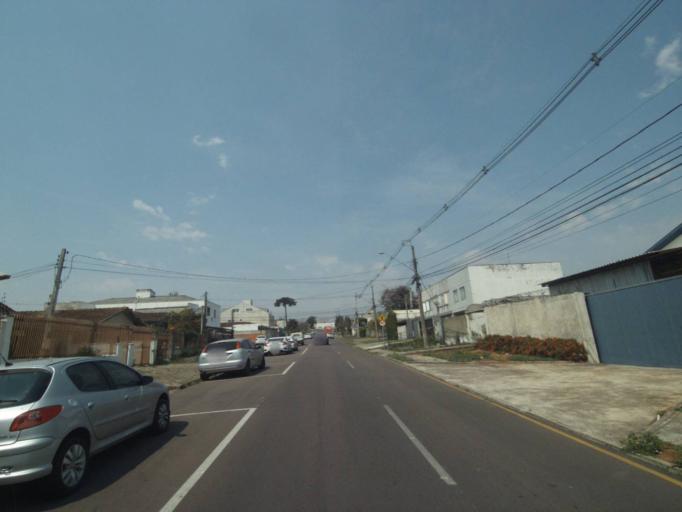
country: BR
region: Parana
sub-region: Curitiba
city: Curitiba
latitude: -25.4616
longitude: -49.2624
